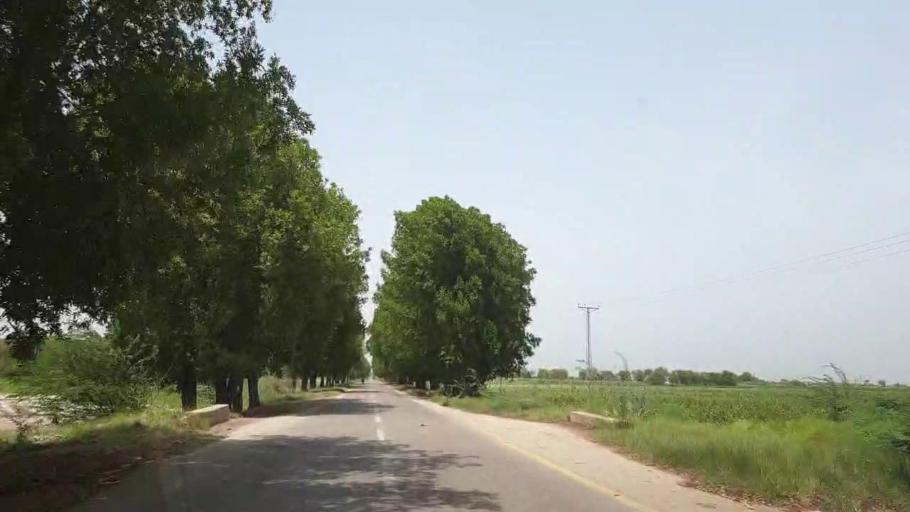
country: PK
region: Sindh
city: Sakrand
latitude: 26.1851
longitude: 68.2319
